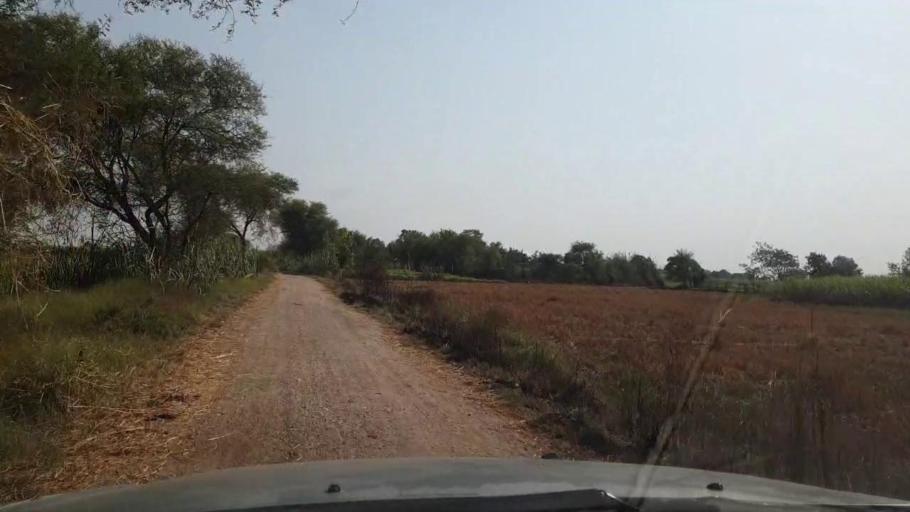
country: PK
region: Sindh
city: Bulri
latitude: 24.9036
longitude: 68.3758
